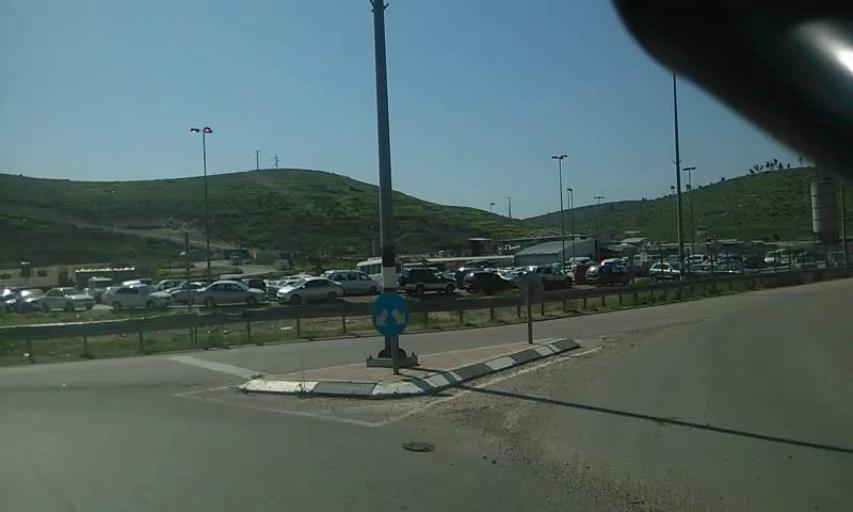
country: PS
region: West Bank
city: Idhna
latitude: 31.5906
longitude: 34.9645
